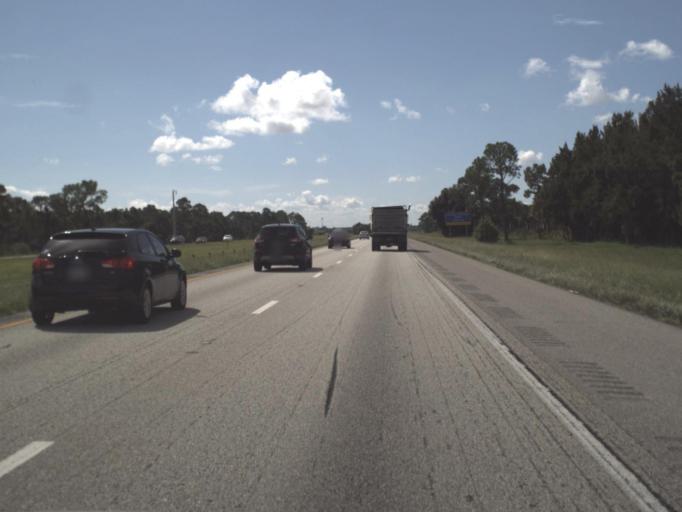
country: US
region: Florida
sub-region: Charlotte County
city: Harbour Heights
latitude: 27.0121
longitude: -82.0437
